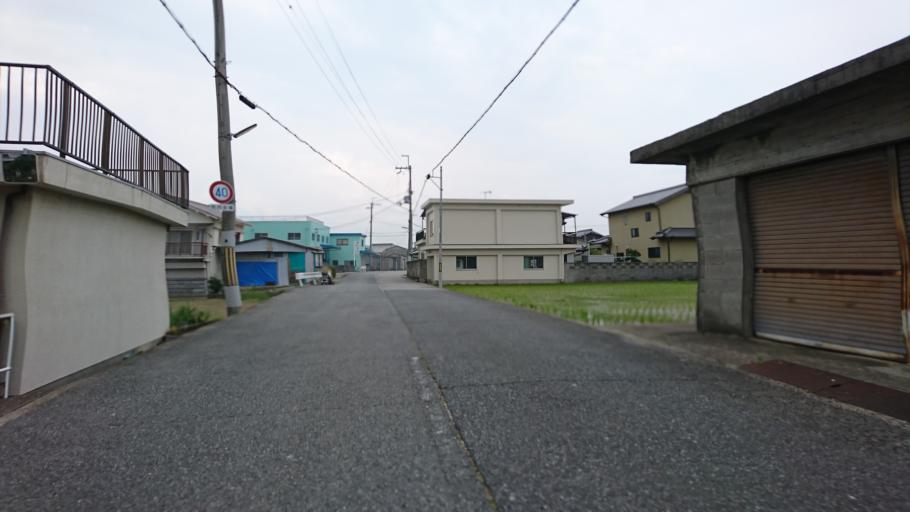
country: JP
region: Hyogo
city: Miki
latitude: 34.7405
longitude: 134.9625
